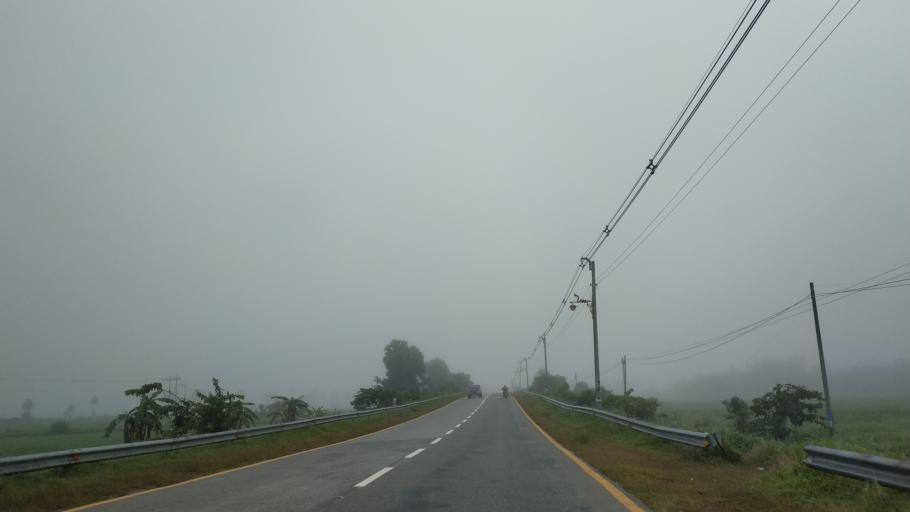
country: MM
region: Tanintharyi
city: Dawei
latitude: 14.1130
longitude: 98.2126
